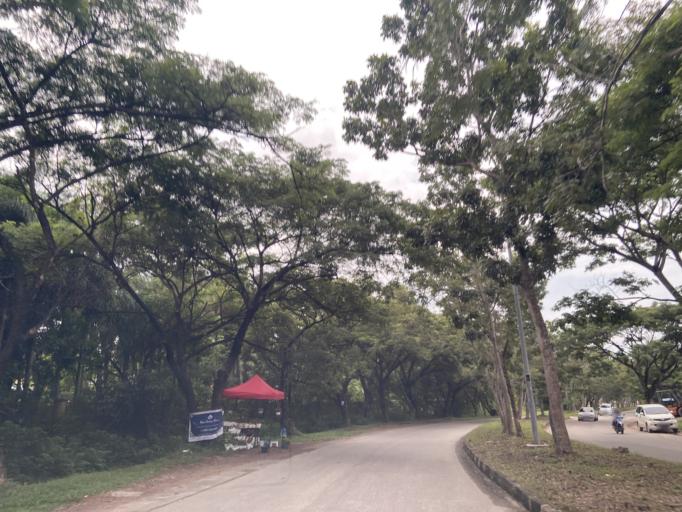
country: SG
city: Singapore
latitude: 1.1268
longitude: 104.0447
